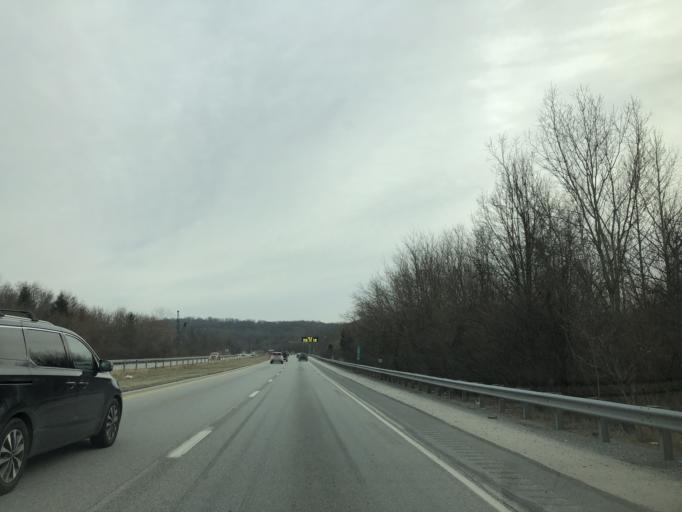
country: US
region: Pennsylvania
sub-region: Chester County
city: Exton
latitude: 40.0149
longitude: -75.6578
